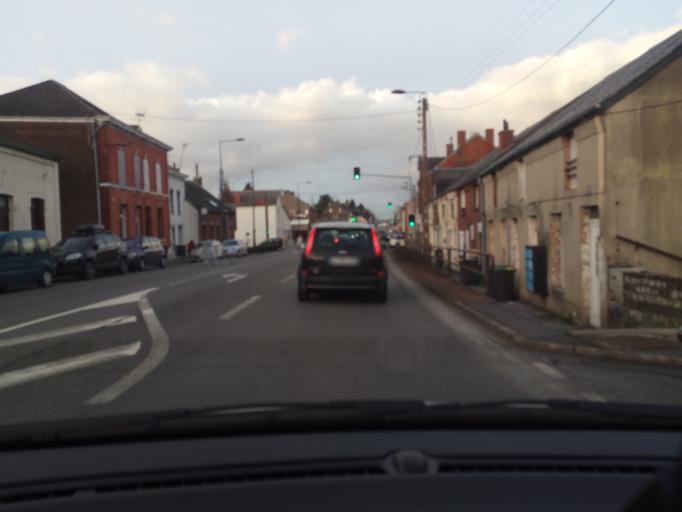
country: FR
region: Nord-Pas-de-Calais
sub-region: Departement du Nord
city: Maubeuge
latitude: 50.2886
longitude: 3.9748
